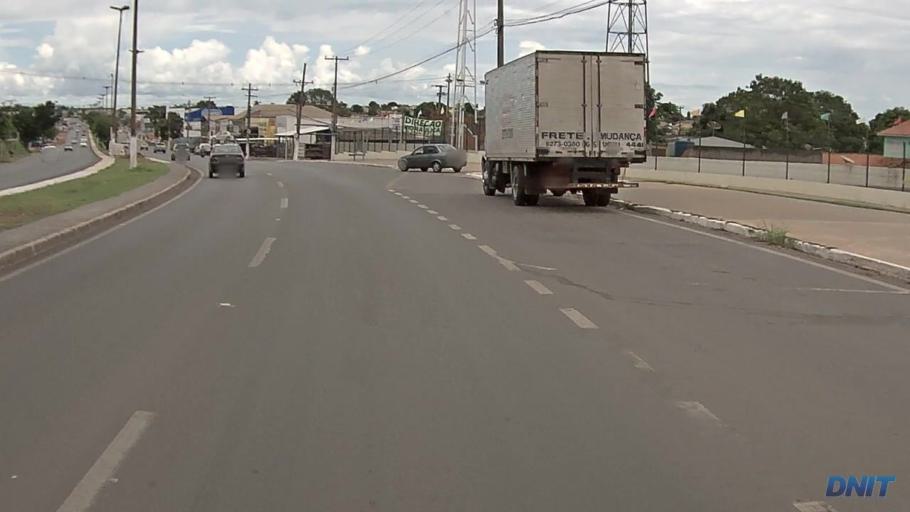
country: BR
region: Mato Grosso
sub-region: Varzea Grande
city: Varzea Grande
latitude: -15.6402
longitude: -56.1693
